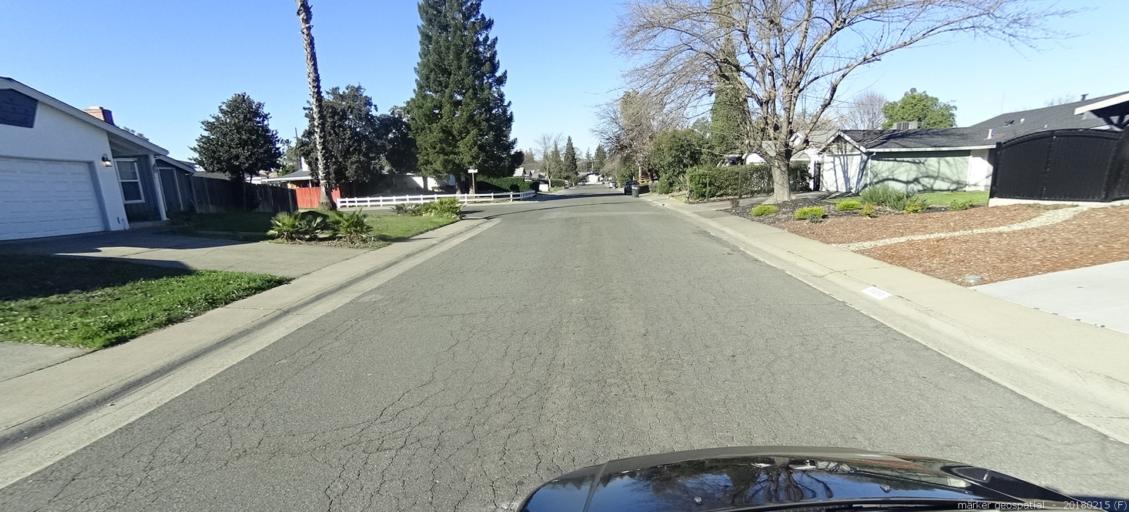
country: US
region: California
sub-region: Sacramento County
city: Foothill Farms
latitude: 38.6673
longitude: -121.3232
